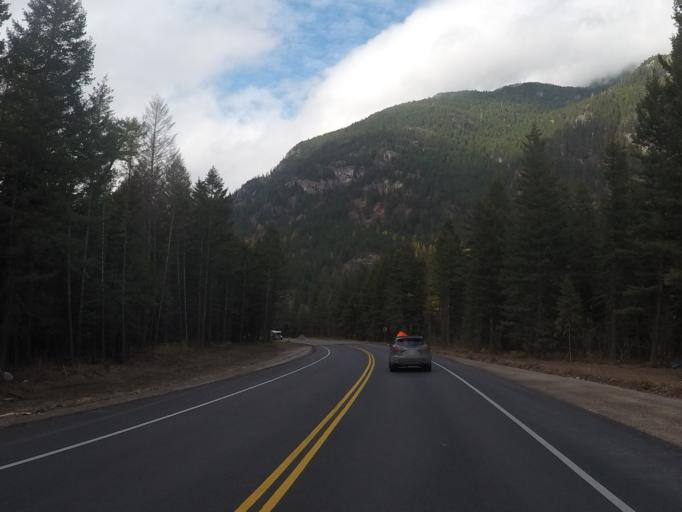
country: US
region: Montana
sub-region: Flathead County
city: Columbia Falls
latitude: 48.3876
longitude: -114.0903
